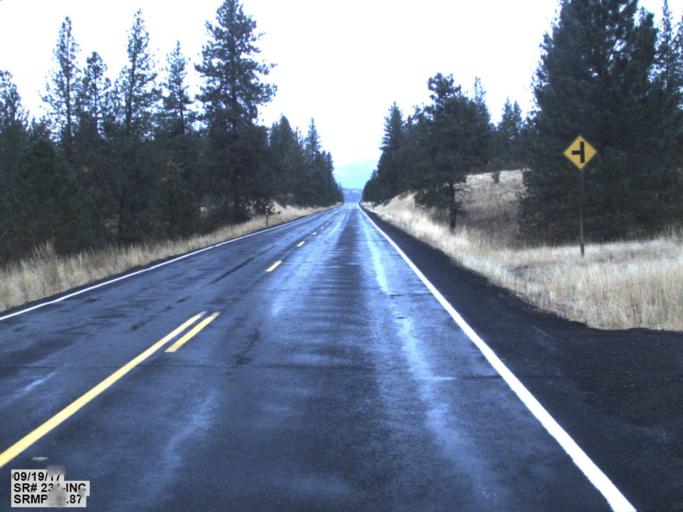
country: US
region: Washington
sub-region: Lincoln County
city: Davenport
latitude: 47.7873
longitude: -117.8897
